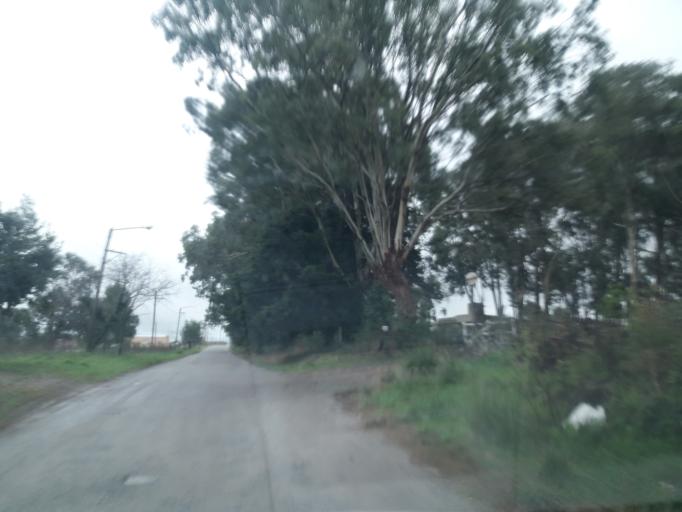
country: AR
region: Buenos Aires
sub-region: Partido de Tandil
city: Tandil
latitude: -37.3295
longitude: -59.1794
